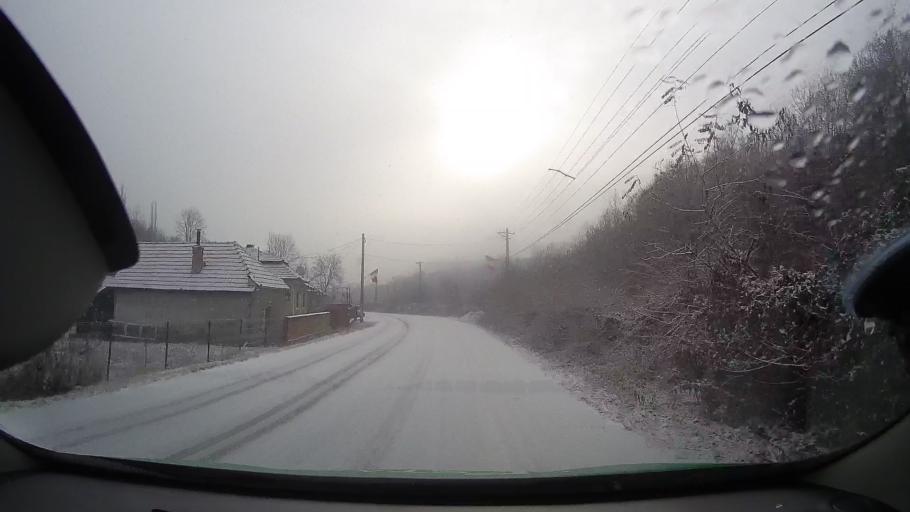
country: RO
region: Alba
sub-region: Comuna Livezile
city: Livezile
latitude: 46.3645
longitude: 23.6079
